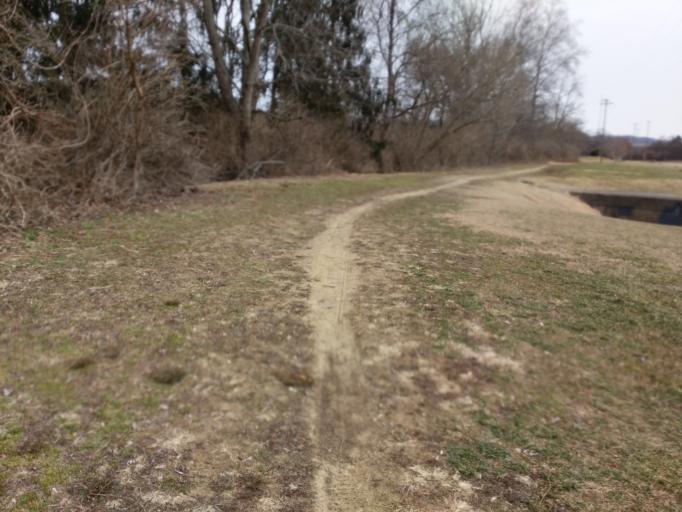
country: US
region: Ohio
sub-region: Athens County
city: Athens
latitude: 39.3336
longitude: -82.0863
